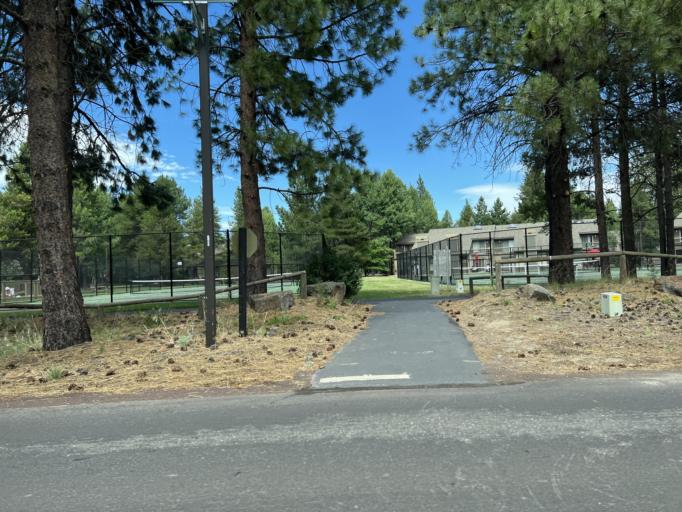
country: US
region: Oregon
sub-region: Deschutes County
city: Sunriver
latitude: 43.8831
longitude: -121.4422
